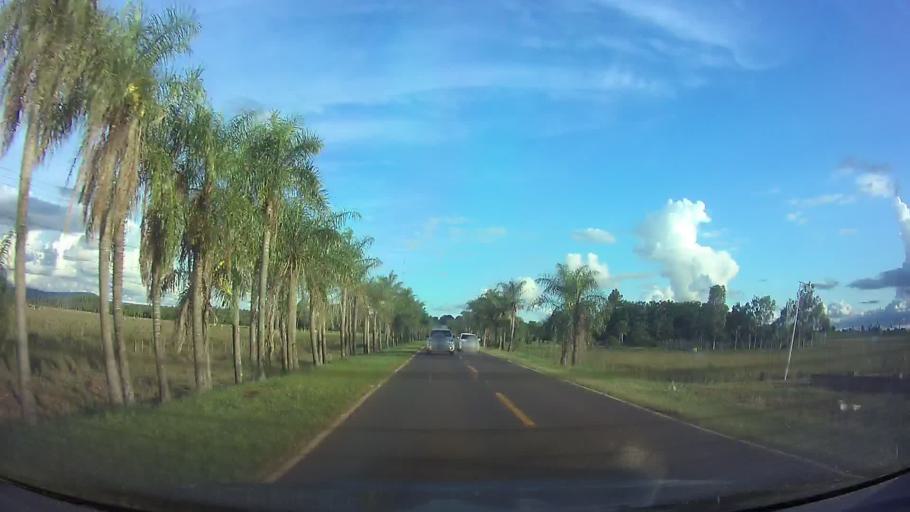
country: PY
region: Paraguari
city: Ybycui
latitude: -26.0034
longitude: -57.0433
